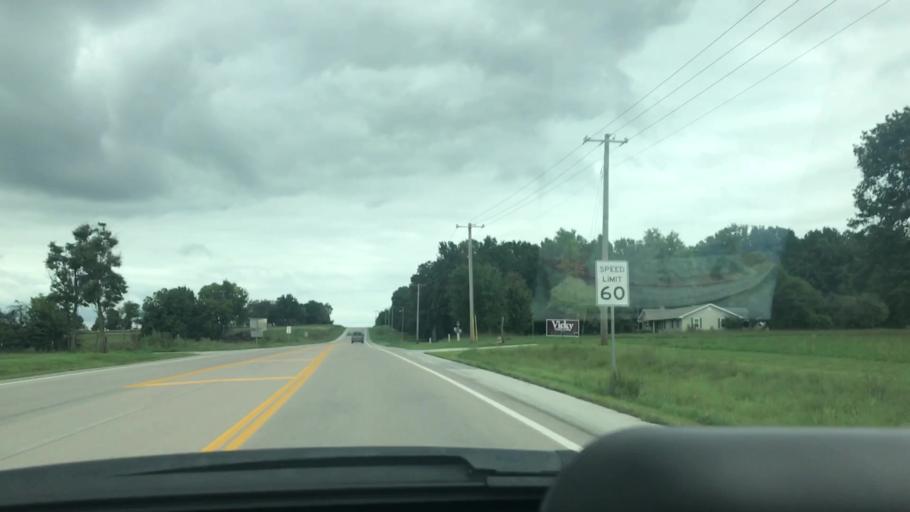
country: US
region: Missouri
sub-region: Dallas County
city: Buffalo
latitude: 37.6690
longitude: -93.1033
